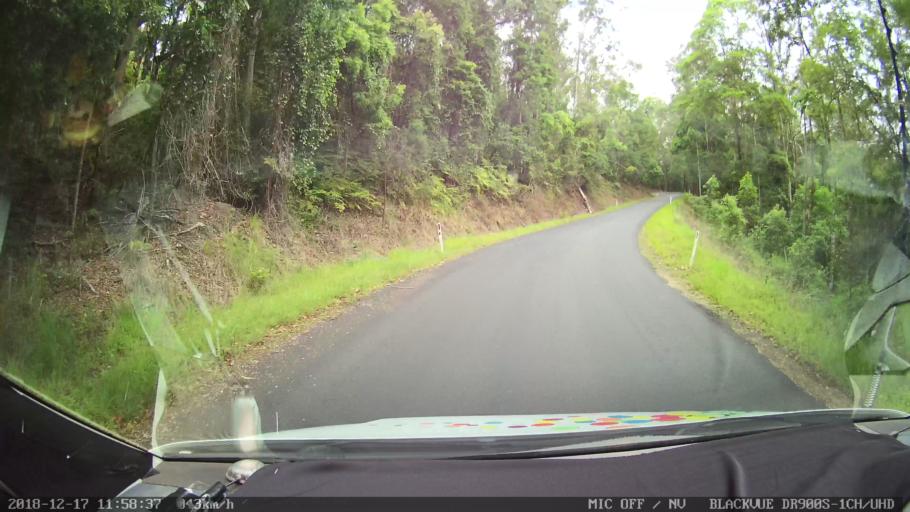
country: AU
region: New South Wales
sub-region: Kyogle
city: Kyogle
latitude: -28.5350
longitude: 152.5698
